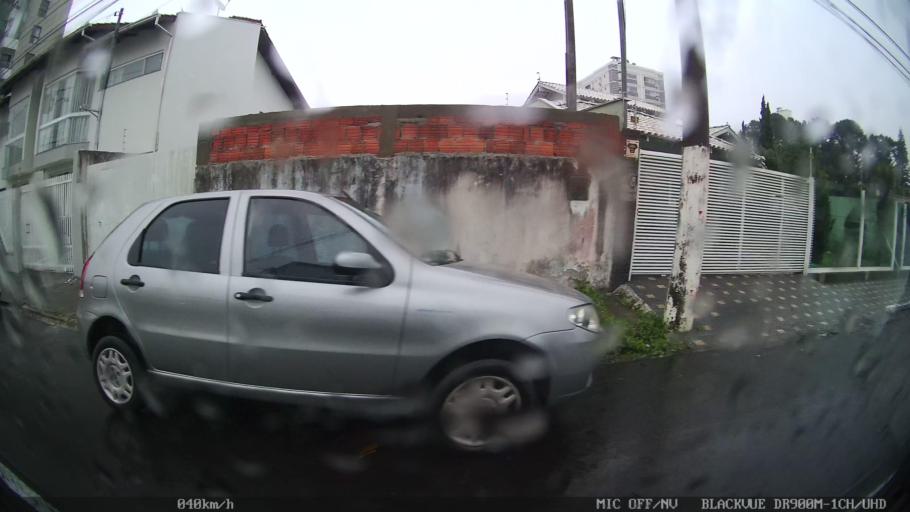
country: BR
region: Santa Catarina
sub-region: Itajai
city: Itajai
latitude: -26.9132
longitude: -48.6703
